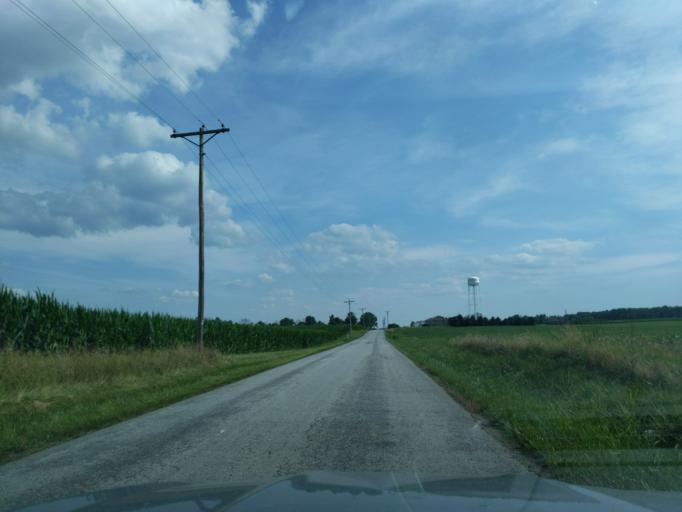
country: US
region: Indiana
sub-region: Decatur County
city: Greensburg
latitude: 39.2769
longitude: -85.4651
